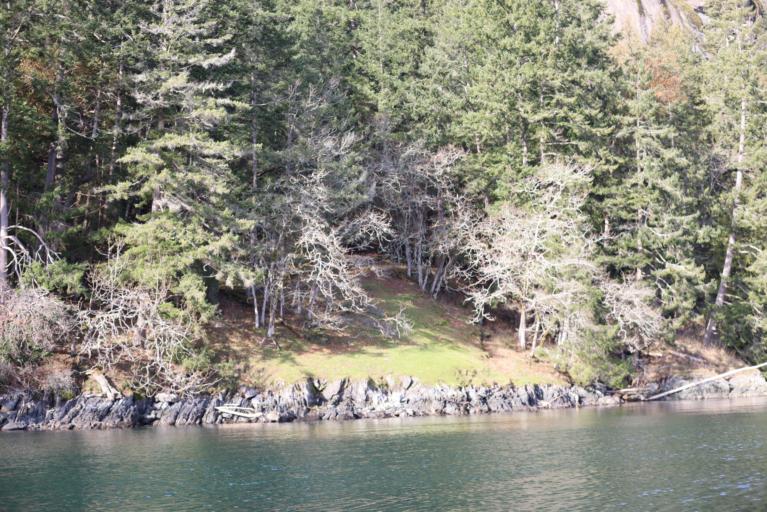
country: CA
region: British Columbia
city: North Cowichan
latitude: 48.7792
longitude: -123.5658
